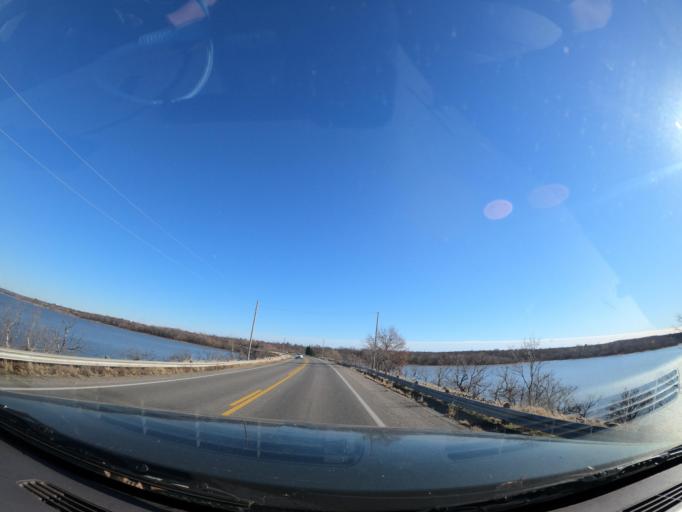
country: US
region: Oklahoma
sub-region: Pittsburg County
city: Longtown
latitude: 35.2411
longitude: -95.5584
